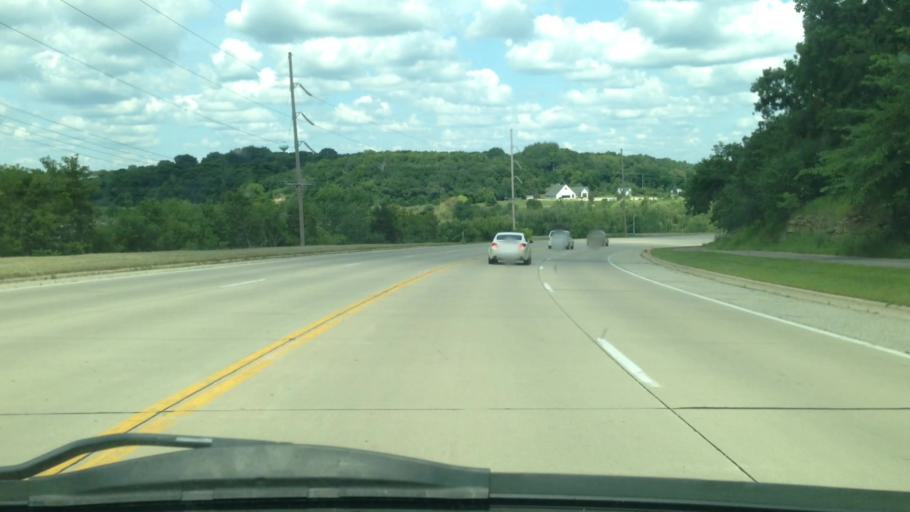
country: US
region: Minnesota
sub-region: Olmsted County
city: Rochester
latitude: 44.0148
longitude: -92.5167
